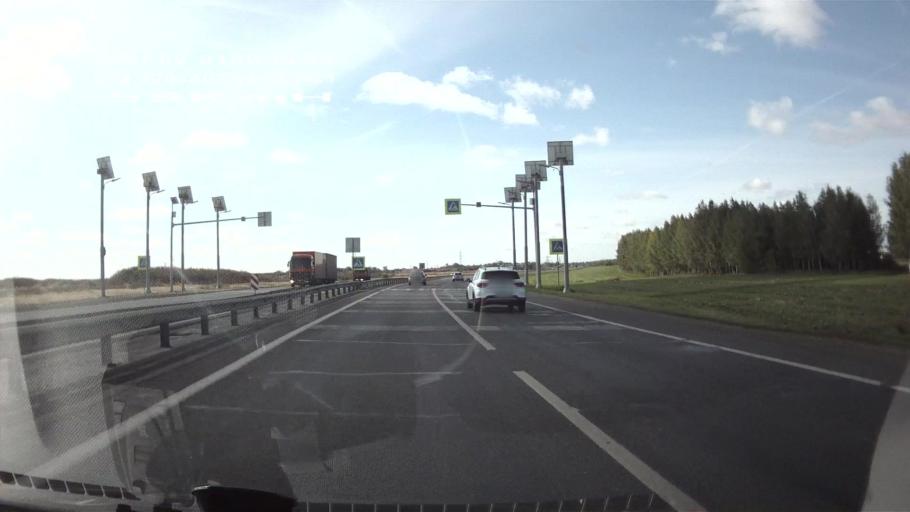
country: RU
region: Ulyanovsk
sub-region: Ulyanovskiy Rayon
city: Ulyanovsk
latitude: 54.2698
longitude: 48.2605
